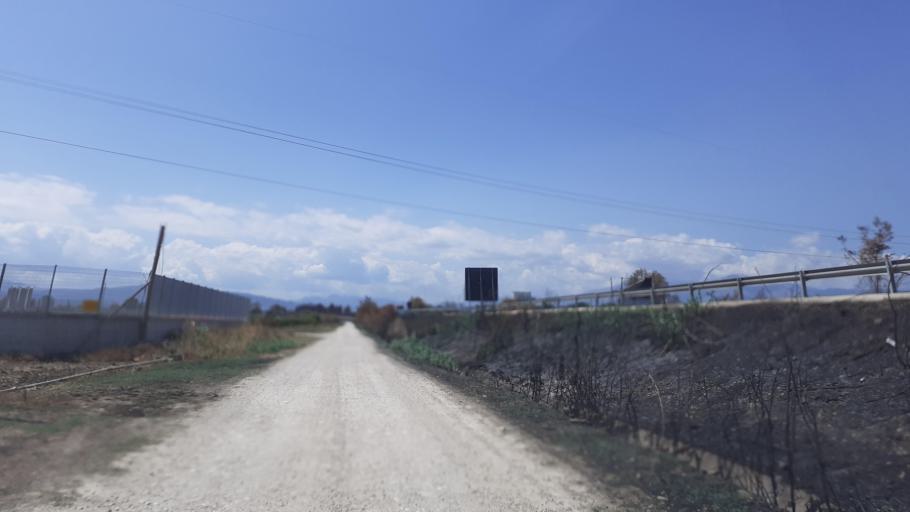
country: IT
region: Abruzzo
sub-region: Provincia di Chieti
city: Fossacesia
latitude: 42.2201
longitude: 14.5010
